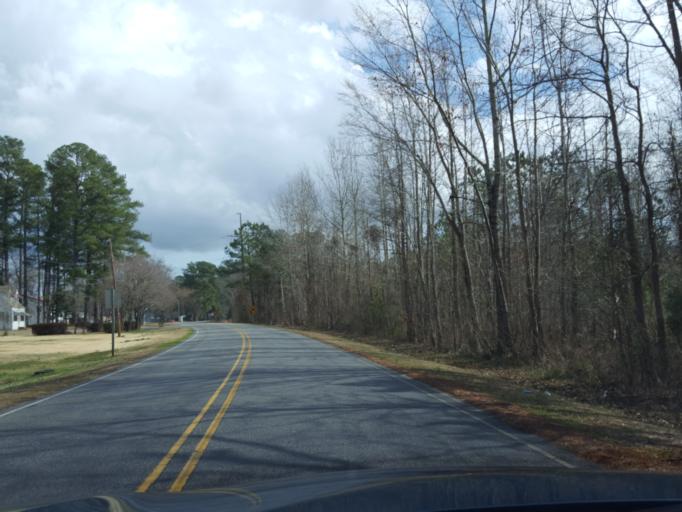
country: US
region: North Carolina
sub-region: Washington County
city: Plymouth
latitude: 35.8672
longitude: -76.7251
